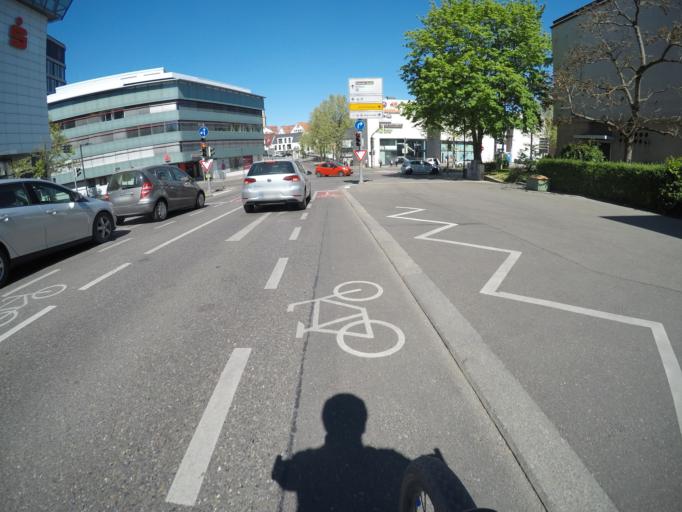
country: DE
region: Baden-Wuerttemberg
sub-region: Regierungsbezirk Stuttgart
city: Waiblingen
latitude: 48.8294
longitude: 9.3150
